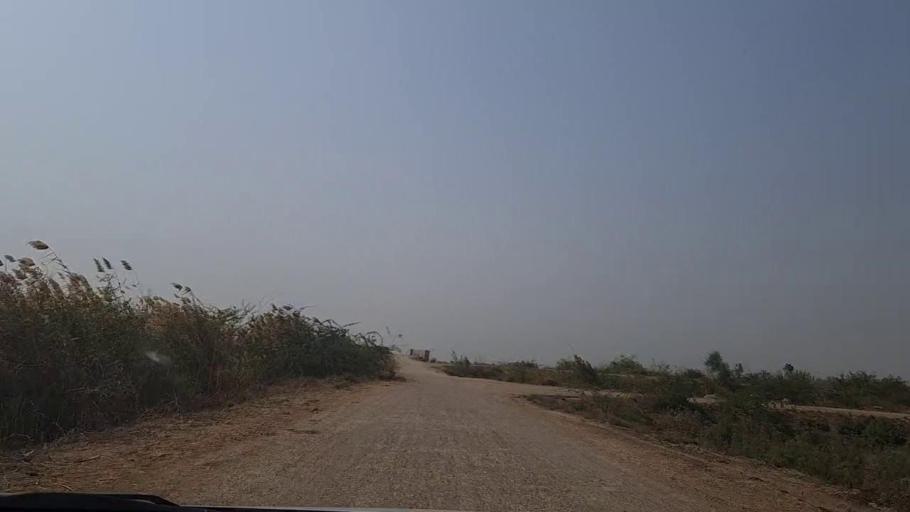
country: PK
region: Sindh
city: Pithoro
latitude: 25.5497
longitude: 69.2144
